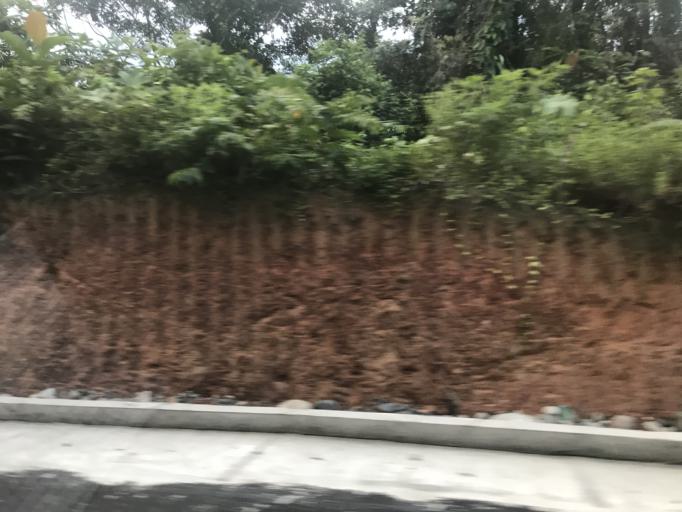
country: EC
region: Napo
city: Tena
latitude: -1.0595
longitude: -77.7001
